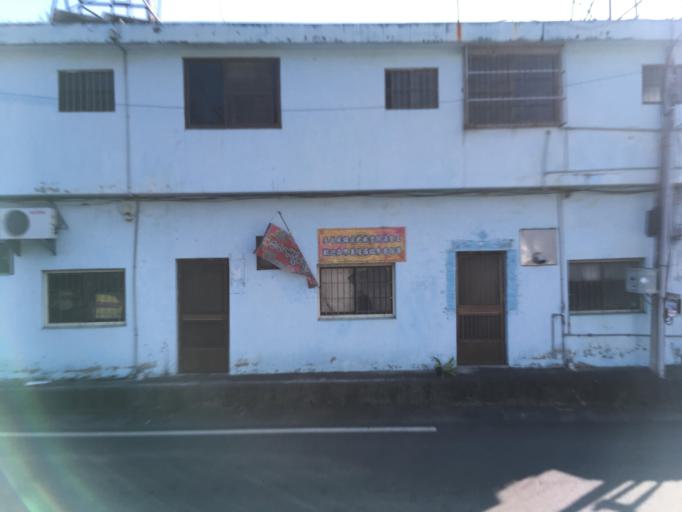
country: TW
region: Taiwan
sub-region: Chiayi
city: Jiayi Shi
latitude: 23.4530
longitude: 120.5565
